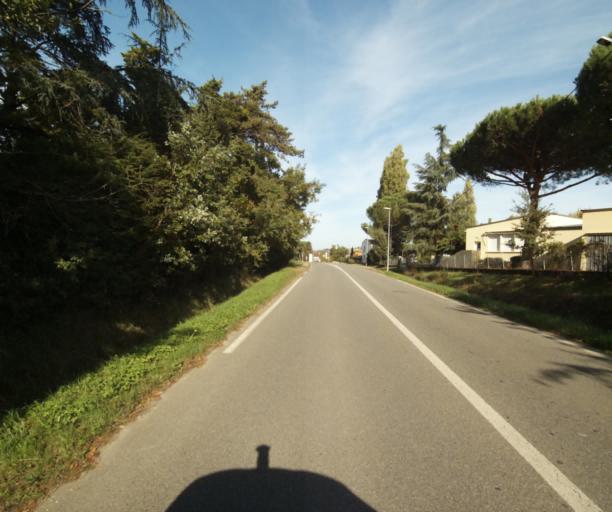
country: FR
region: Midi-Pyrenees
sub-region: Departement du Tarn-et-Garonne
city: Nohic
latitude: 43.9067
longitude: 1.4512
